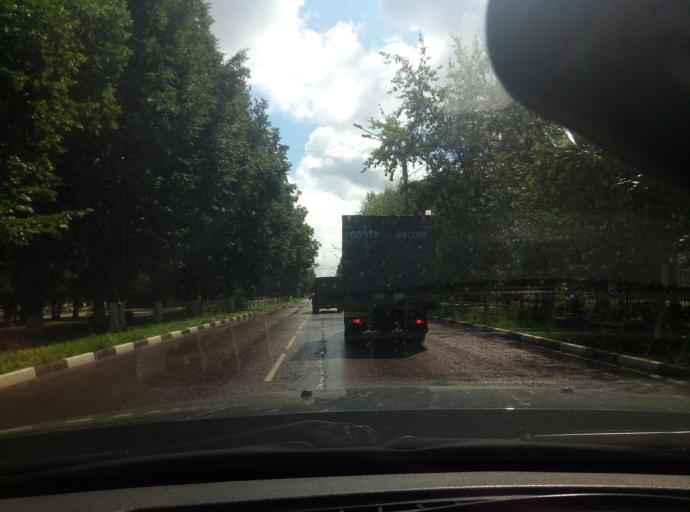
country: RU
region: Tula
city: Novomoskovsk
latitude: 54.0086
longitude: 38.2961
